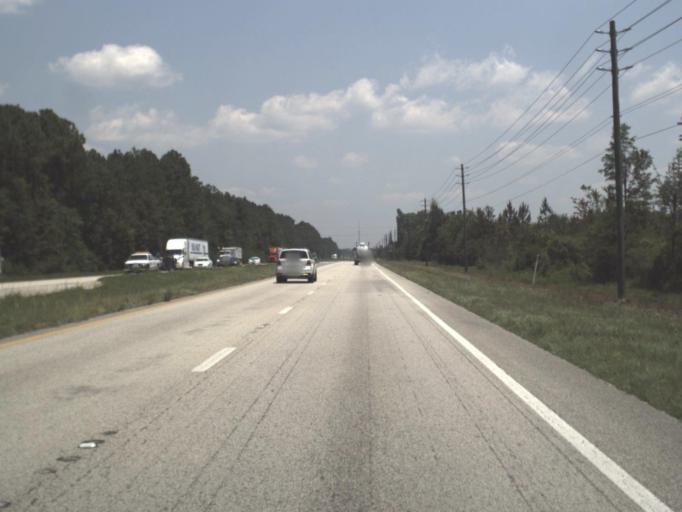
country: US
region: Florida
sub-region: Duval County
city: Baldwin
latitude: 30.2687
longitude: -81.9888
